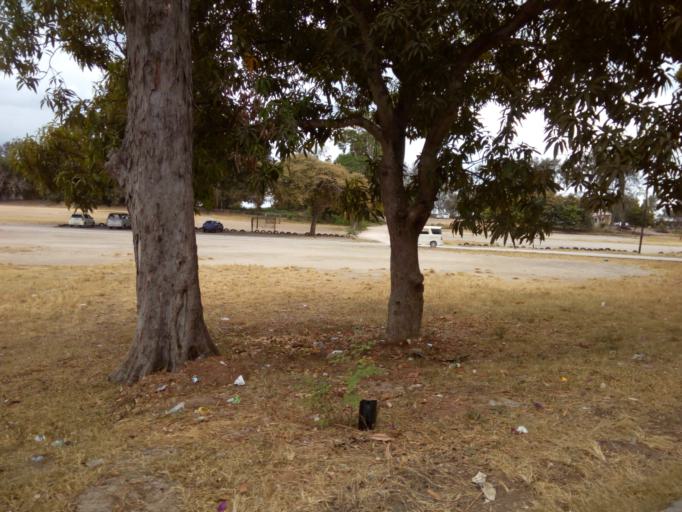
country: TZ
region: Zanzibar Urban/West
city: Zanzibar
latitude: -6.1732
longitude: 39.1963
